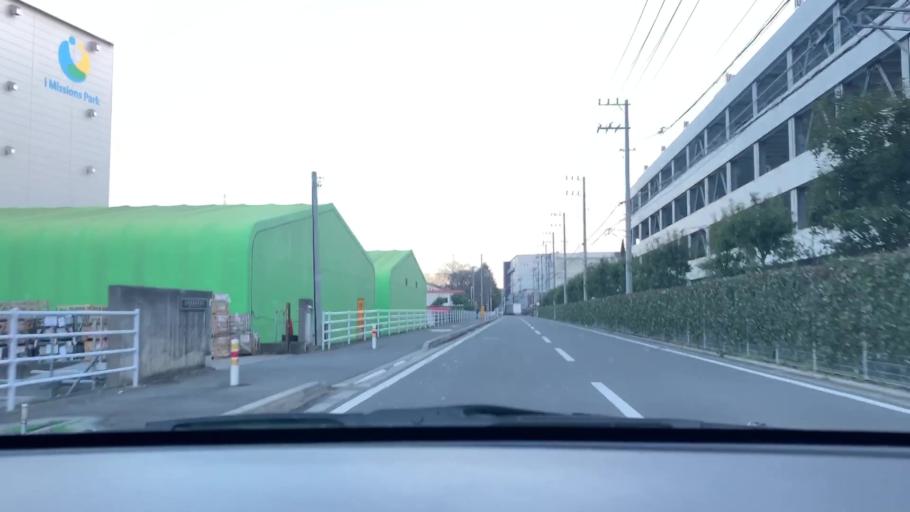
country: JP
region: Chiba
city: Kashiwa
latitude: 35.9088
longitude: 139.9455
